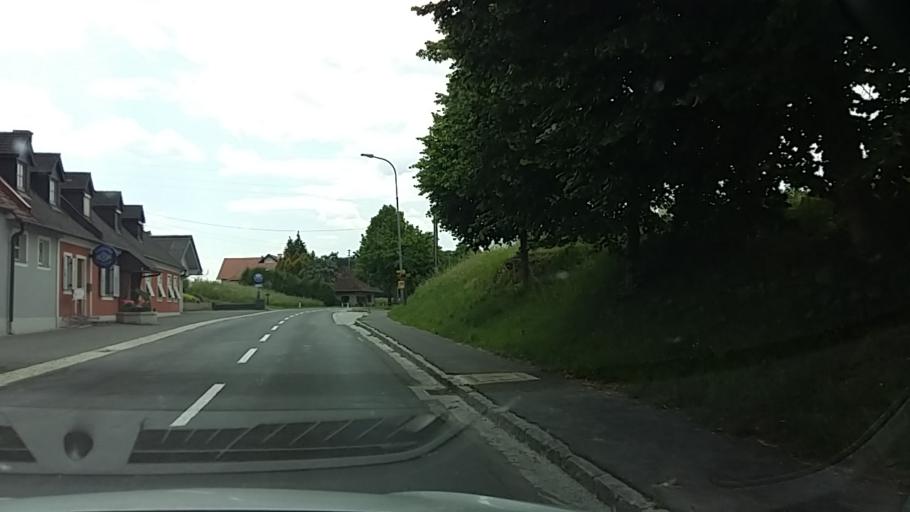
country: AT
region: Styria
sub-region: Politischer Bezirk Hartberg-Fuerstenfeld
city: Hainersdorf
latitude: 47.0938
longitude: 15.9563
